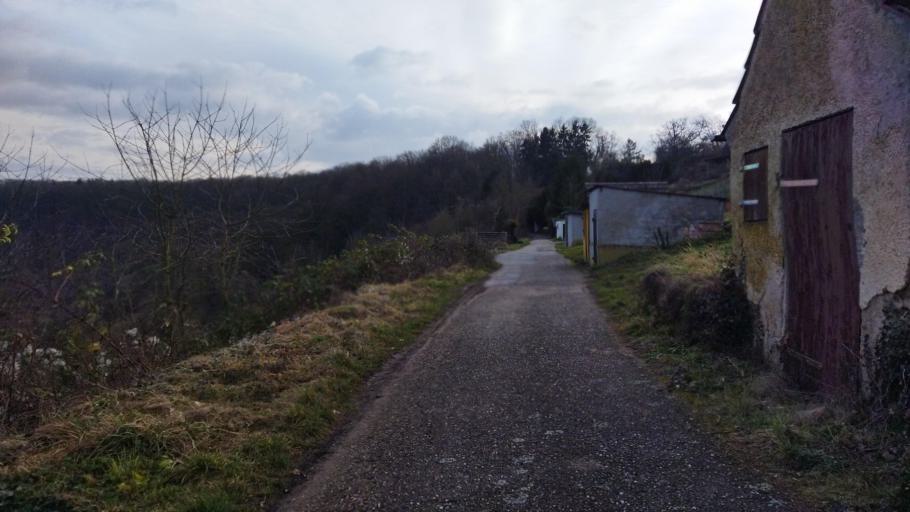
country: DE
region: Baden-Wuerttemberg
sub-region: Regierungsbezirk Stuttgart
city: Hessigheim
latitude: 48.9904
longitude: 9.1685
